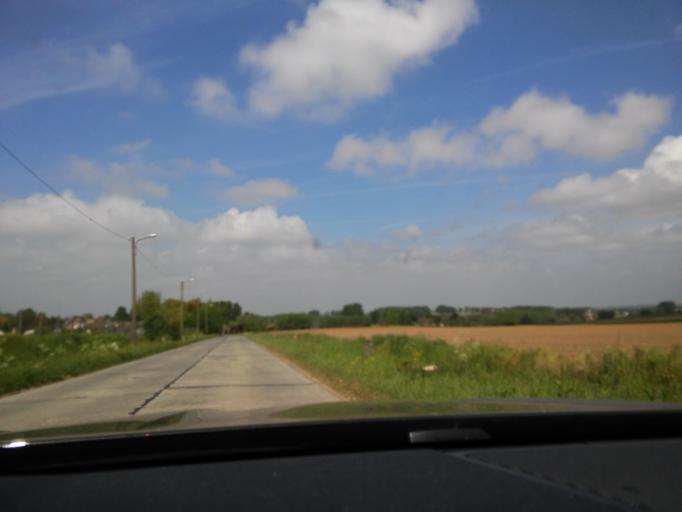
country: BE
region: Wallonia
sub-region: Province du Brabant Wallon
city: Tubize
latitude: 50.7206
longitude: 4.1785
